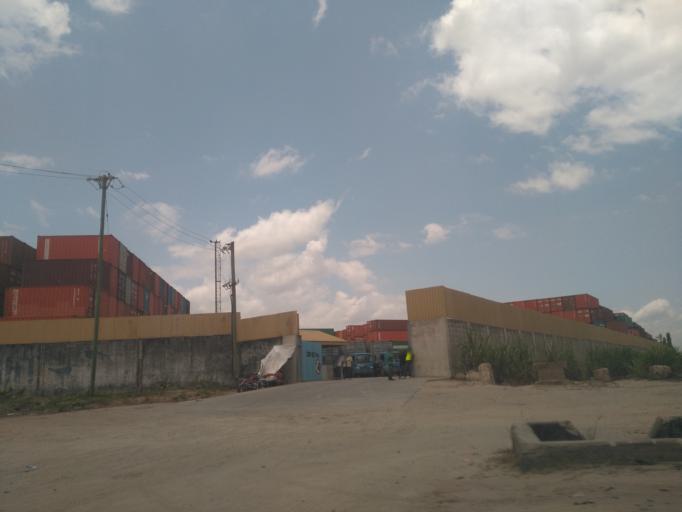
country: TZ
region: Dar es Salaam
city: Dar es Salaam
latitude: -6.8471
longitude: 39.2919
